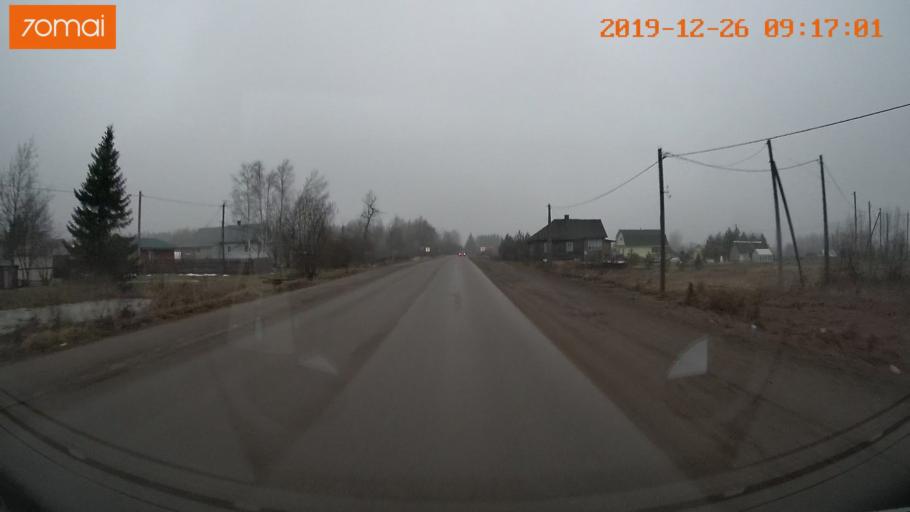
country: RU
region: Vologda
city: Gryazovets
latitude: 58.9251
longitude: 40.2390
